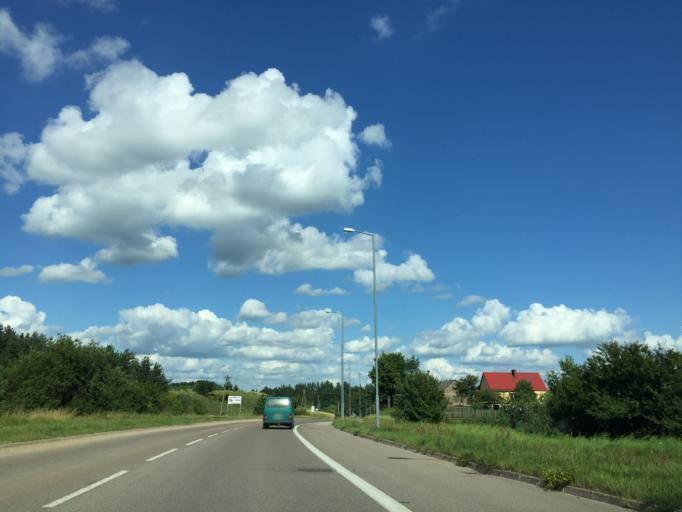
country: PL
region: Podlasie
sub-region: Suwalki
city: Suwalki
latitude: 54.1134
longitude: 22.9603
